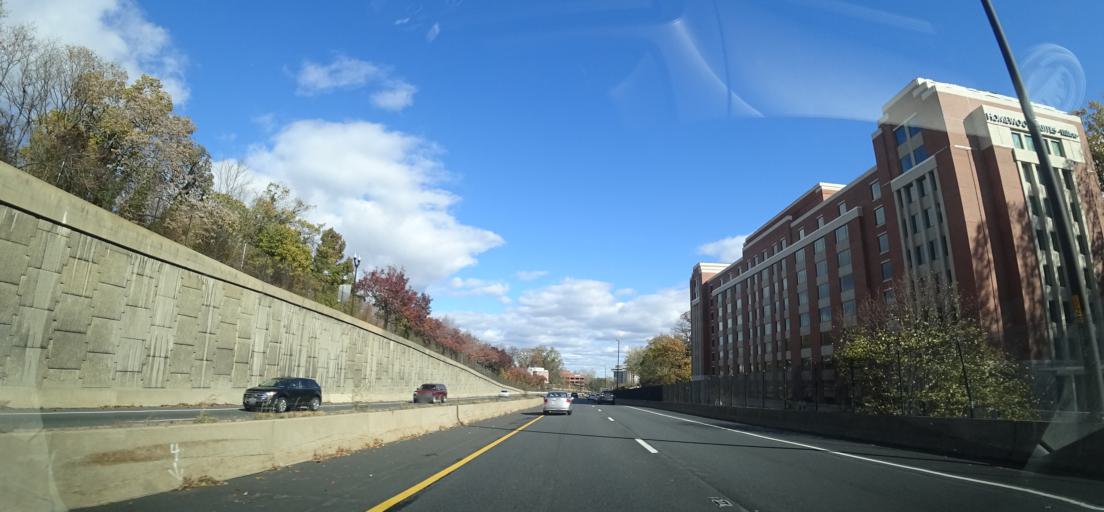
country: US
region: Virginia
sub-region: Arlington County
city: Arlington
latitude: 38.8970
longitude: -77.0802
